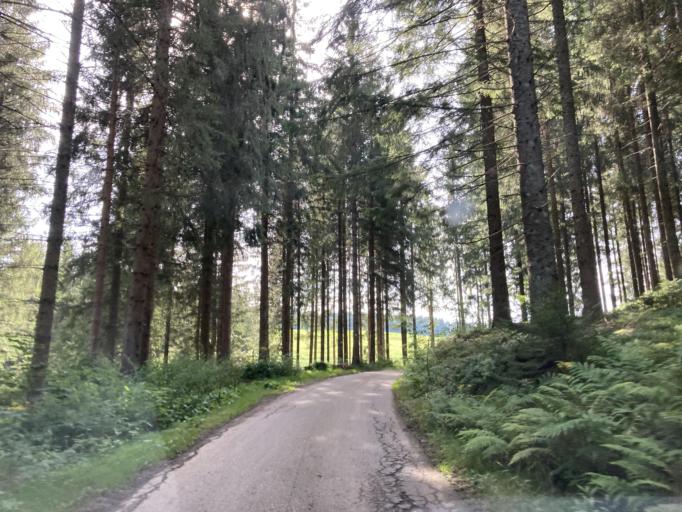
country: DE
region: Baden-Wuerttemberg
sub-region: Freiburg Region
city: Schonwald im Schwarzwald
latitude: 48.0902
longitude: 8.2333
